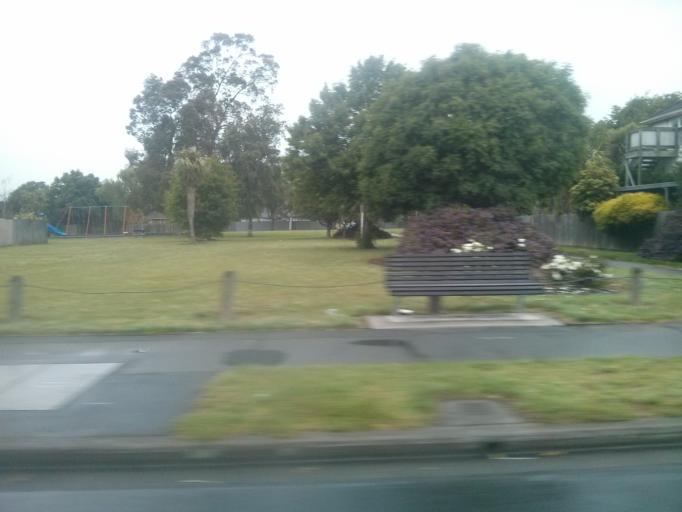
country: NZ
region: Canterbury
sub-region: Christchurch City
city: Christchurch
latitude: -43.5315
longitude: 172.5773
